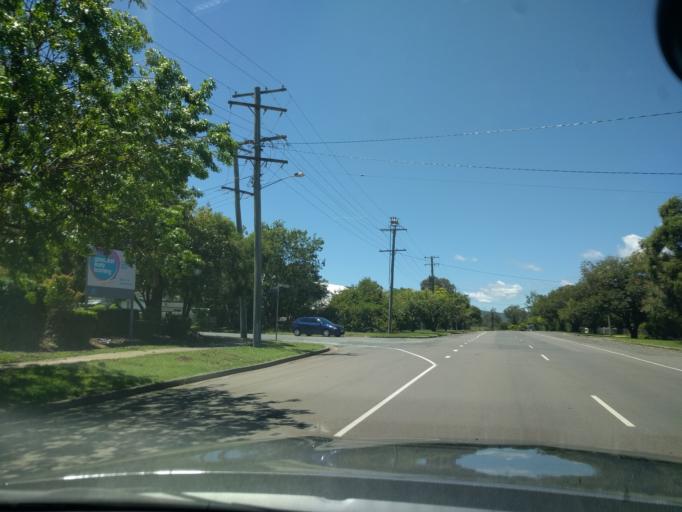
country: AU
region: Queensland
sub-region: Logan
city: Cedar Vale
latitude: -27.9923
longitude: 152.9964
